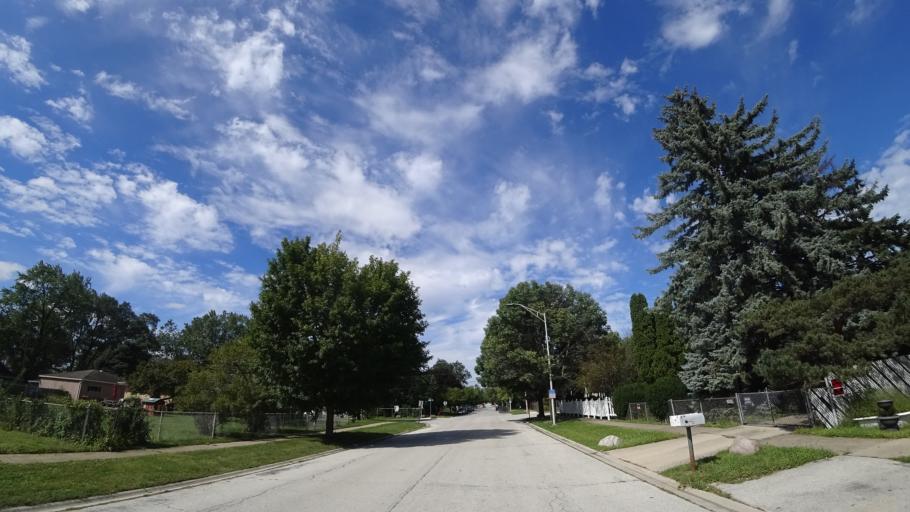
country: US
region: Illinois
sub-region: Cook County
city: Chicago Ridge
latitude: 41.7100
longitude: -87.7746
